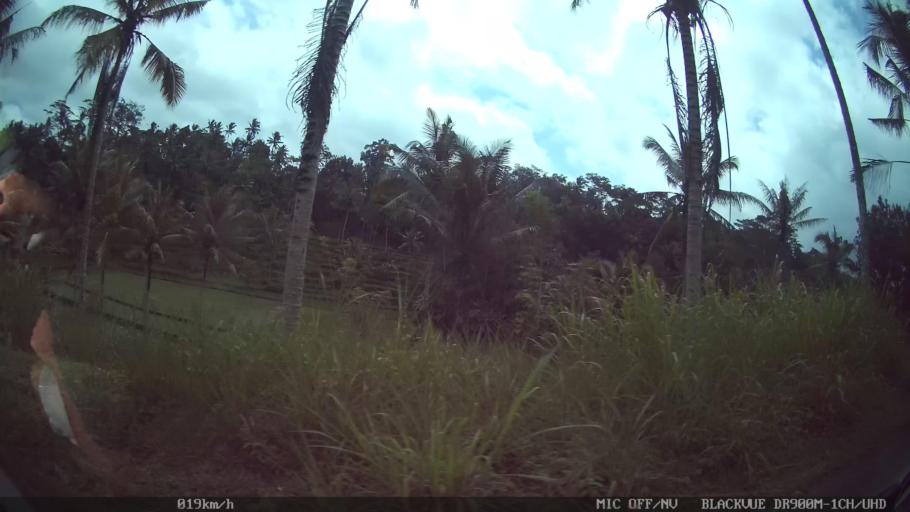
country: ID
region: Bali
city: Banjar Petak
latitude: -8.4480
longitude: 115.3272
